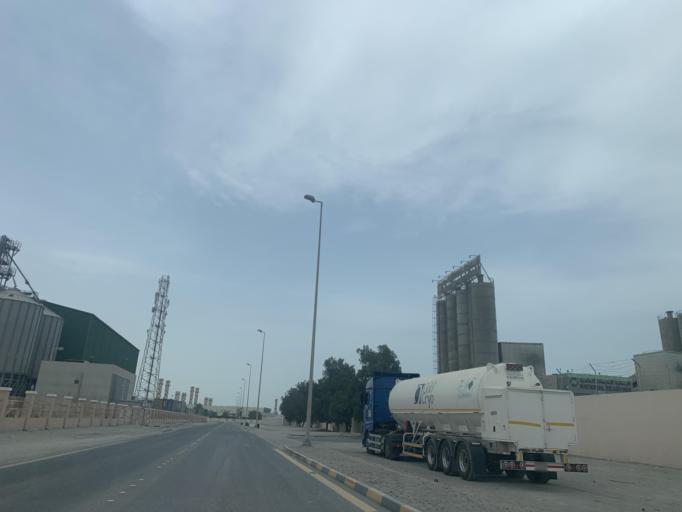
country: BH
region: Muharraq
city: Al Hadd
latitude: 26.2081
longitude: 50.6623
